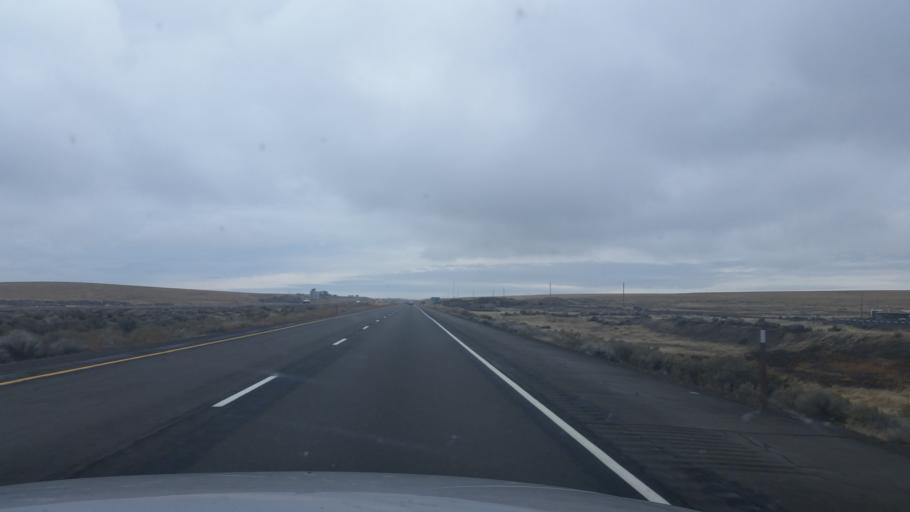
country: US
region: Washington
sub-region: Adams County
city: Ritzville
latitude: 47.1114
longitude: -118.4092
